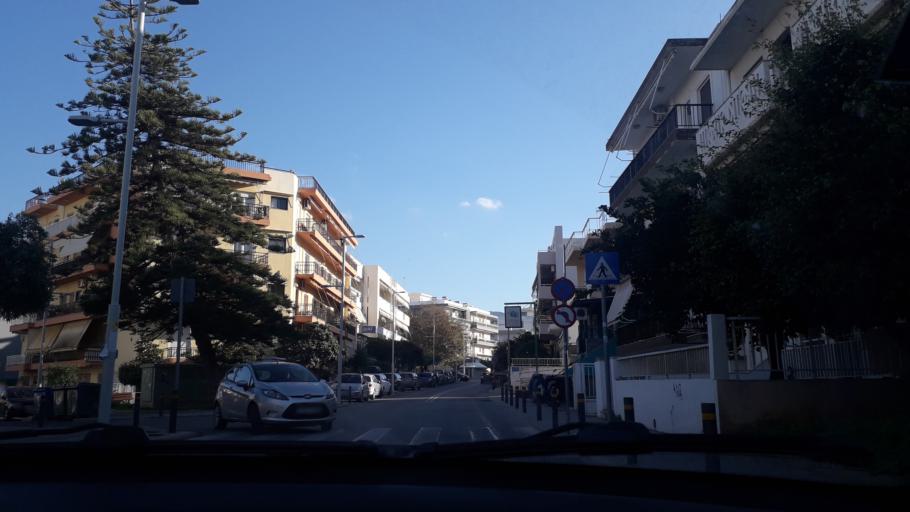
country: GR
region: Crete
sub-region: Nomos Rethymnis
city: Rethymno
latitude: 35.3641
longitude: 24.4713
